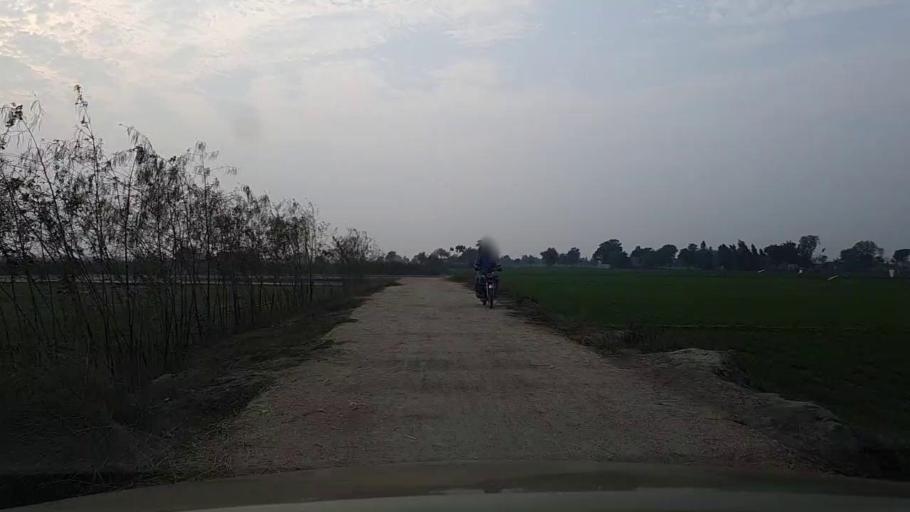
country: PK
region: Sindh
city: Sanghar
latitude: 26.2308
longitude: 68.9418
